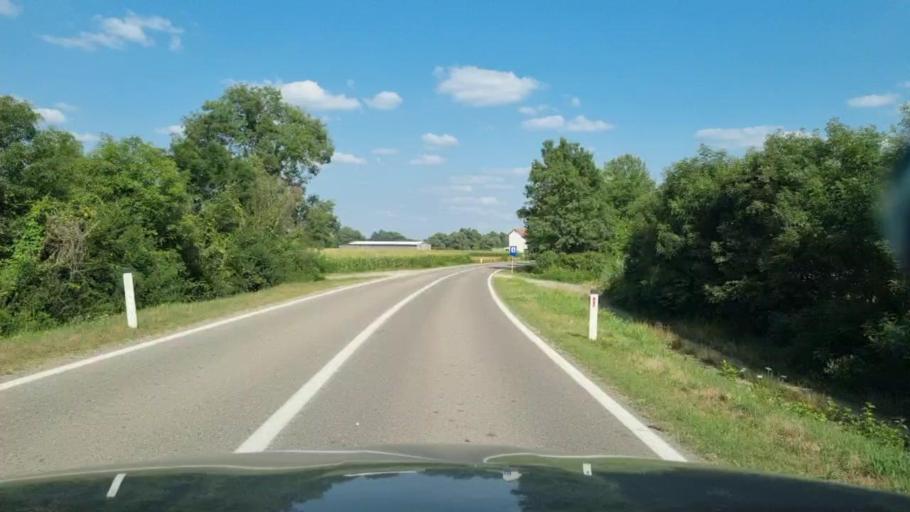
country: BA
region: Federation of Bosnia and Herzegovina
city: Odzak
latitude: 45.1077
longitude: 18.2835
